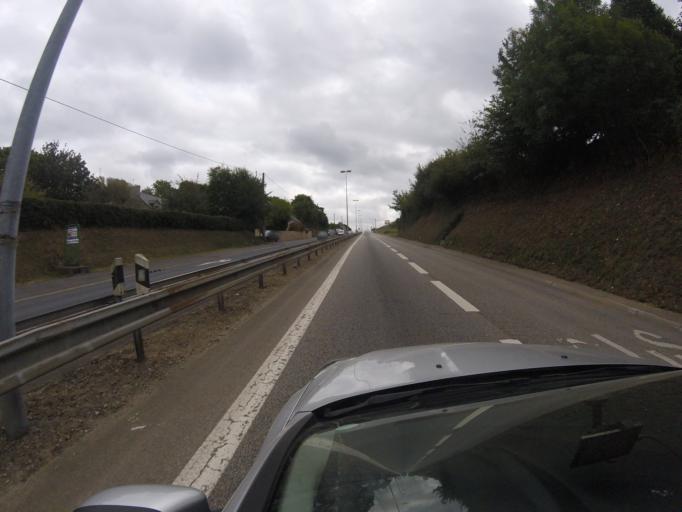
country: FR
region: Lower Normandy
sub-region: Departement de la Manche
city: La Glacerie
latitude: 49.6113
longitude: -1.6008
